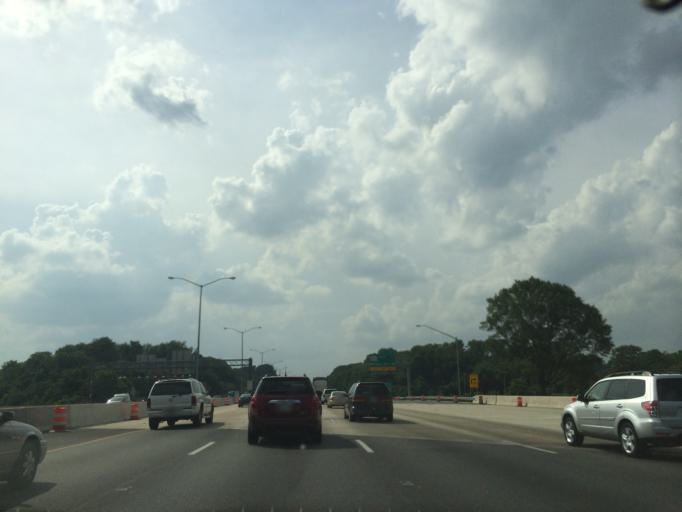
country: US
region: Maryland
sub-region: Baltimore County
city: Charlestown
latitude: 39.2620
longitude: -76.7059
